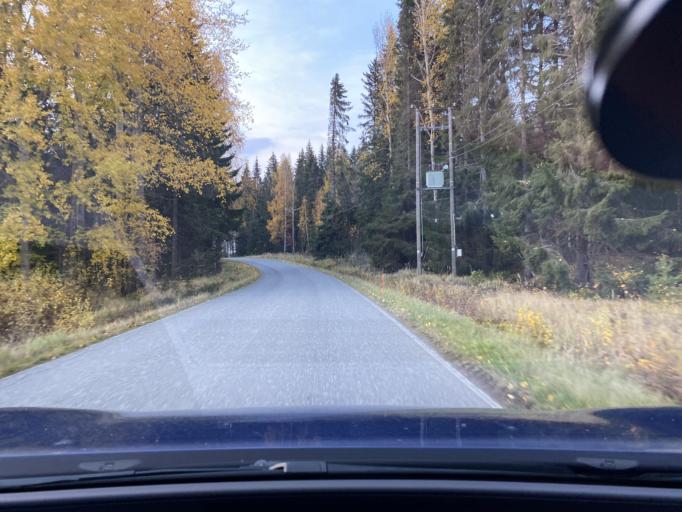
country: FI
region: Pirkanmaa
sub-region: Lounais-Pirkanmaa
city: Punkalaidun
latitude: 61.0740
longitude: 22.9692
